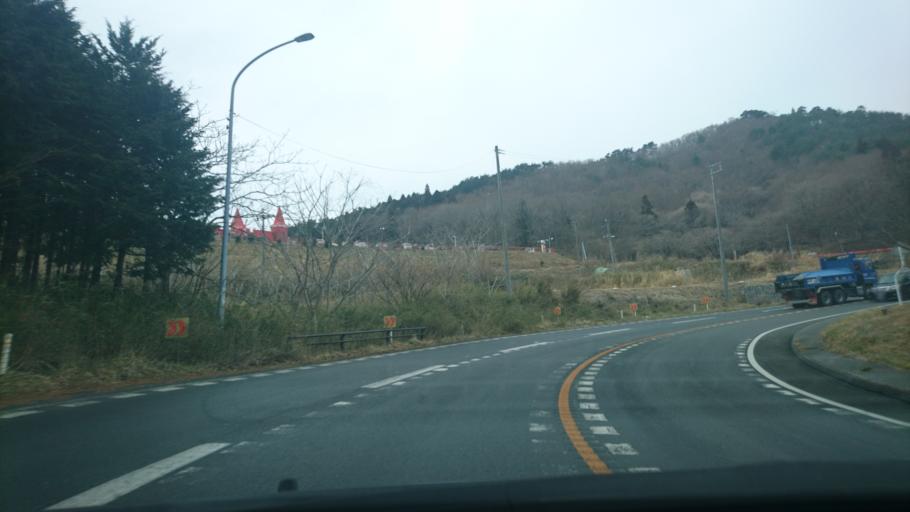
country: JP
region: Iwate
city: Ofunato
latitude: 39.0249
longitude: 141.6903
